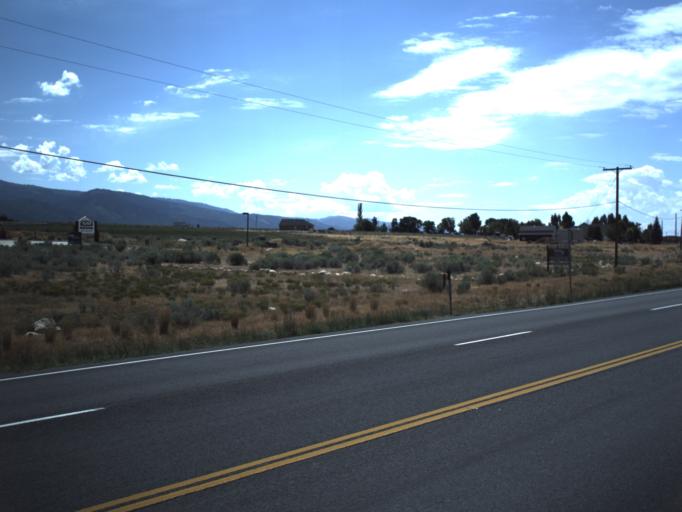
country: US
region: Utah
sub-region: Sanpete County
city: Mount Pleasant
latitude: 39.5306
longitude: -111.4652
